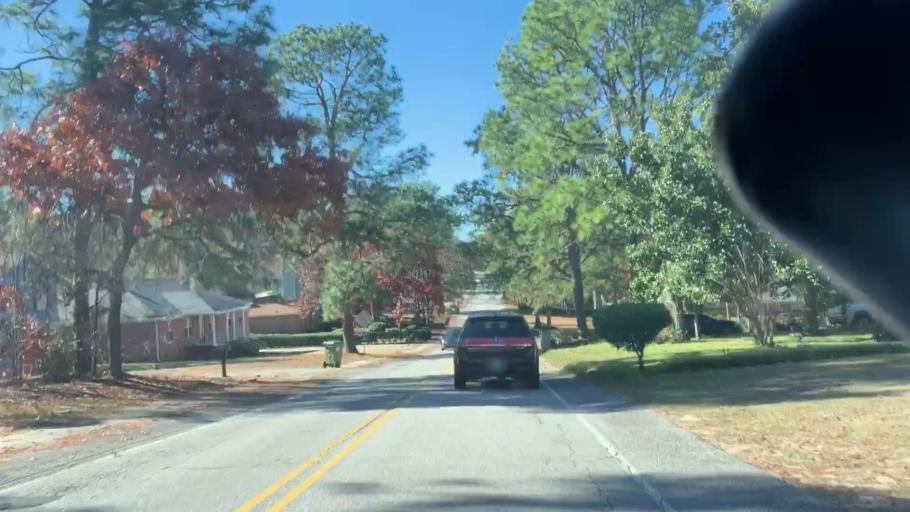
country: US
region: South Carolina
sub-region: Richland County
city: Woodfield
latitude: 34.0641
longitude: -80.9328
